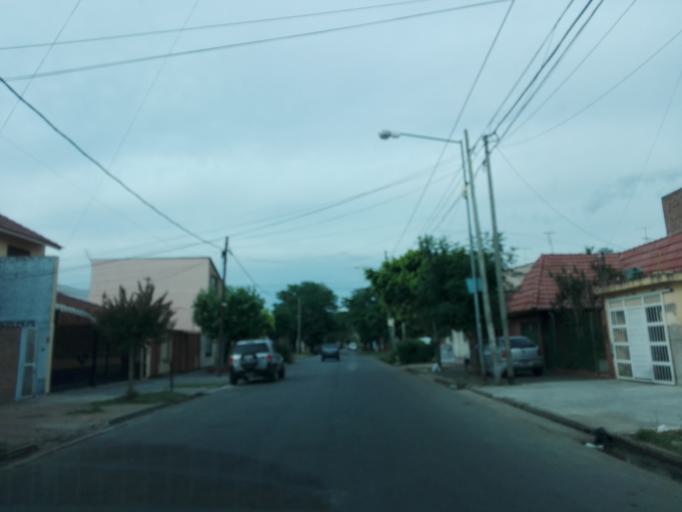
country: AR
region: Buenos Aires
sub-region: Partido de Lanus
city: Lanus
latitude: -34.7182
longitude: -58.3809
